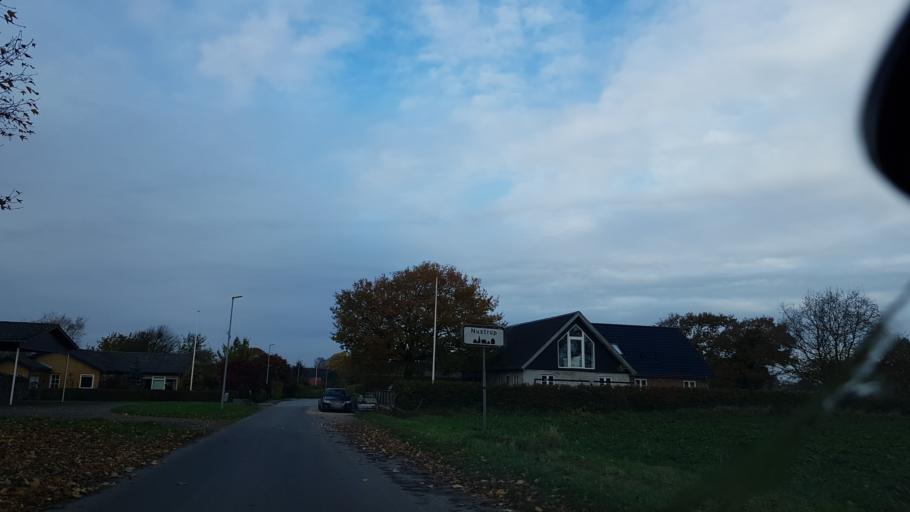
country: DK
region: South Denmark
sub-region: Haderslev Kommune
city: Vojens
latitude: 55.2658
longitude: 9.1875
